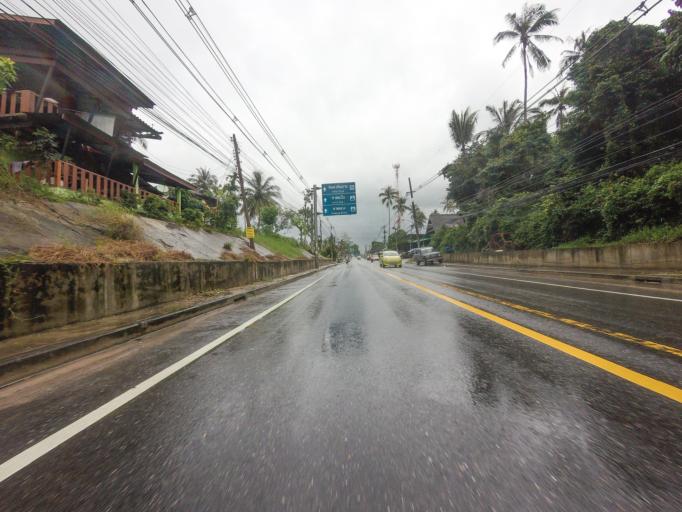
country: TH
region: Surat Thani
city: Ko Samui
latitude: 9.4589
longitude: 99.9872
